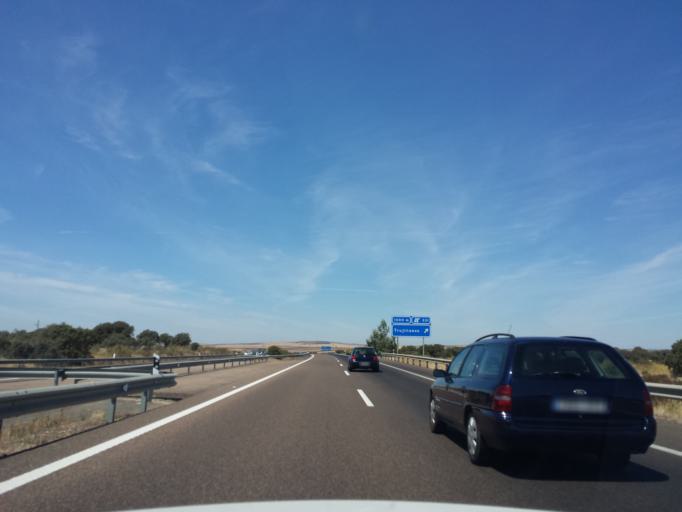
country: ES
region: Extremadura
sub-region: Provincia de Badajoz
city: Trujillanos
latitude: 38.9516
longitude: -6.2276
